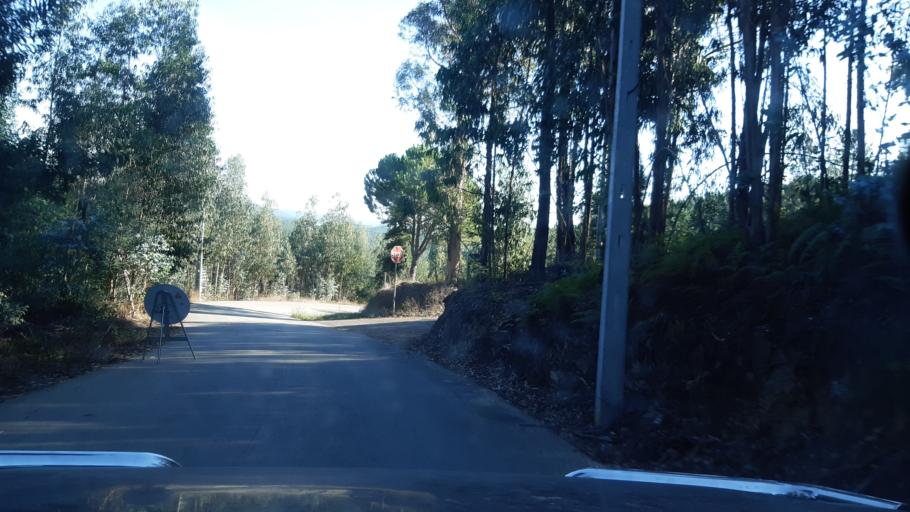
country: PT
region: Aveiro
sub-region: Agueda
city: Aguada de Cima
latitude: 40.5683
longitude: -8.3638
